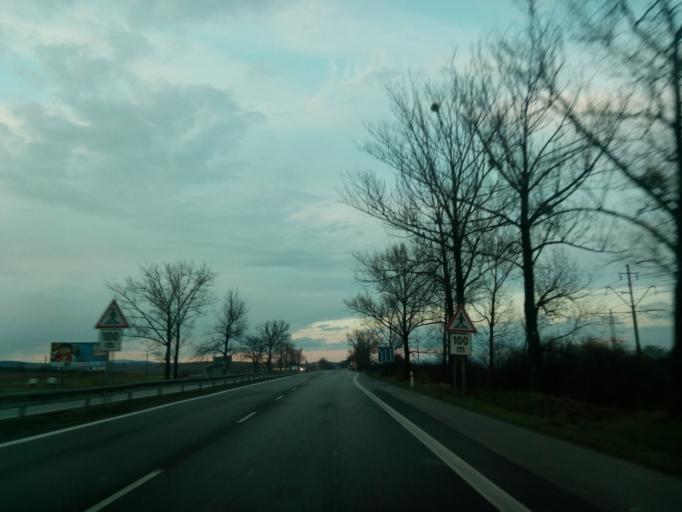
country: SK
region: Kosicky
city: Kosice
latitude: 48.6605
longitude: 21.2073
